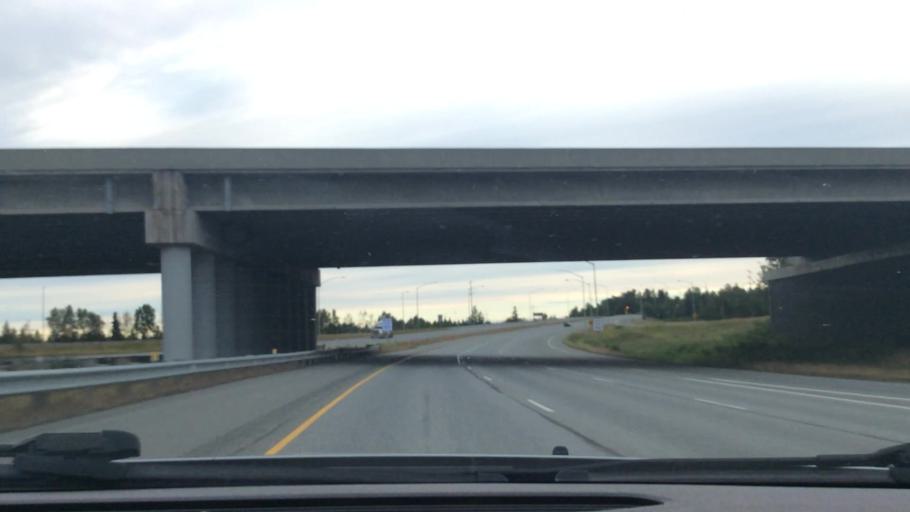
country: US
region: Alaska
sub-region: Anchorage Municipality
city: Anchorage
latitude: 61.1720
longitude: -149.9168
